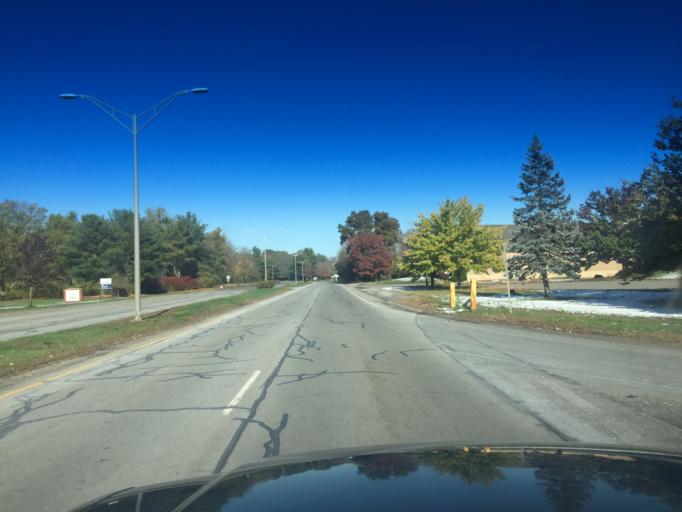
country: US
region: Massachusetts
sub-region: Bristol County
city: Norton
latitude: 41.9481
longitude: -71.1410
